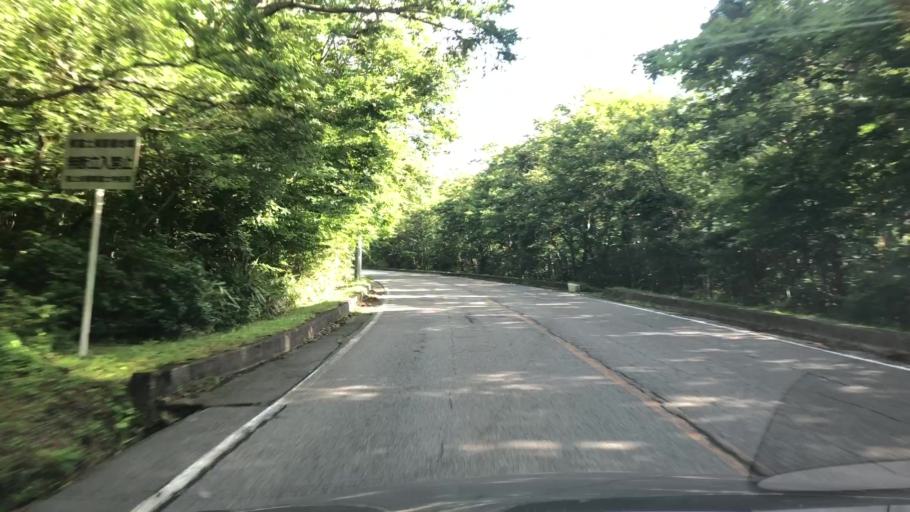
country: JP
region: Shizuoka
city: Gotemba
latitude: 35.3313
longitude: 138.8100
